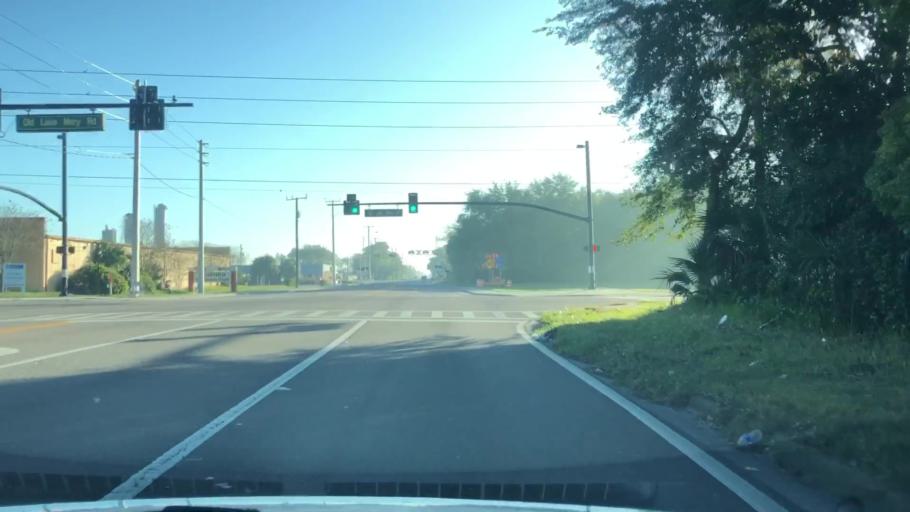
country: US
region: Florida
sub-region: Seminole County
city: Sanford
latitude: 28.7865
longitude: -81.2938
